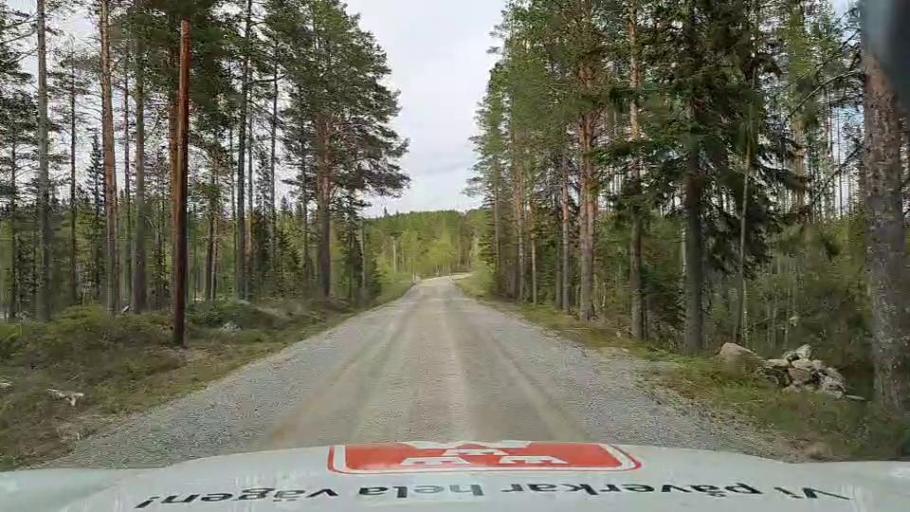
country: SE
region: Jaemtland
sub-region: OEstersunds Kommun
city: Brunflo
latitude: 62.5947
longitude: 14.9135
